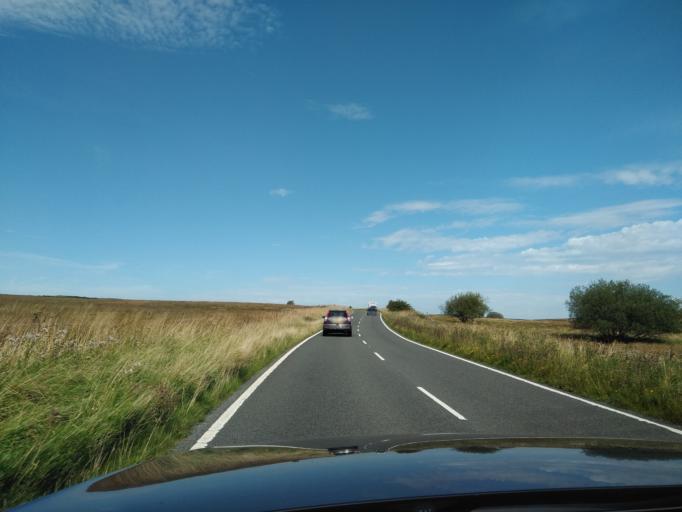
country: GB
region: England
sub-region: Derbyshire
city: Hathersage
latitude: 53.3030
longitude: -1.5920
